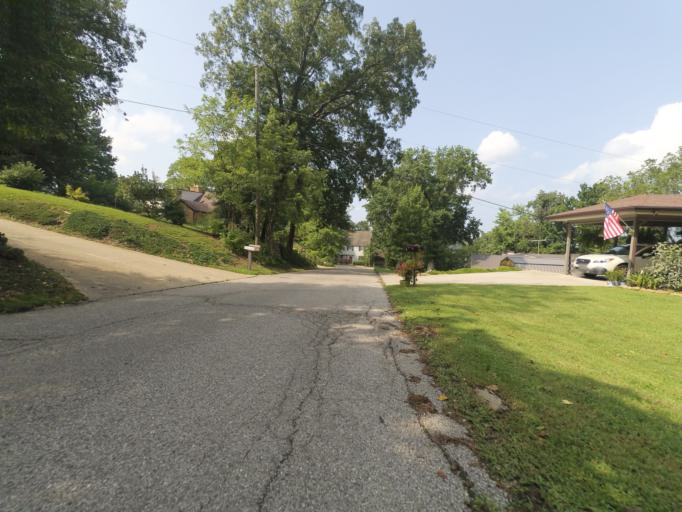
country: US
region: West Virginia
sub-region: Cabell County
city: Huntington
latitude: 38.3982
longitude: -82.4065
